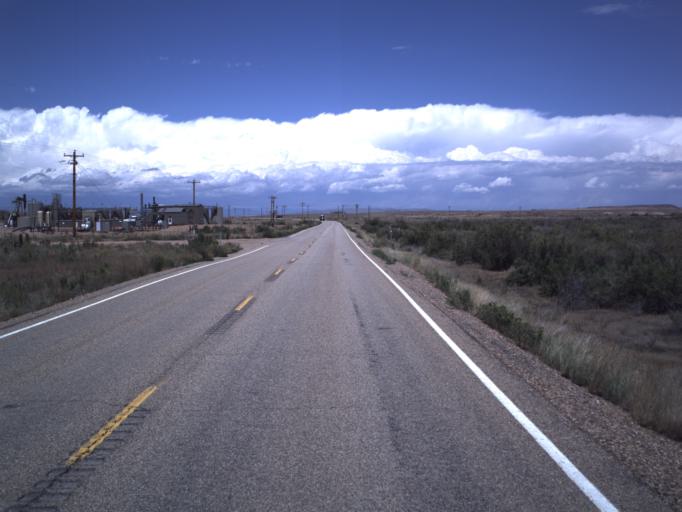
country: US
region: Utah
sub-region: Uintah County
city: Naples
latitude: 40.1185
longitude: -109.6663
